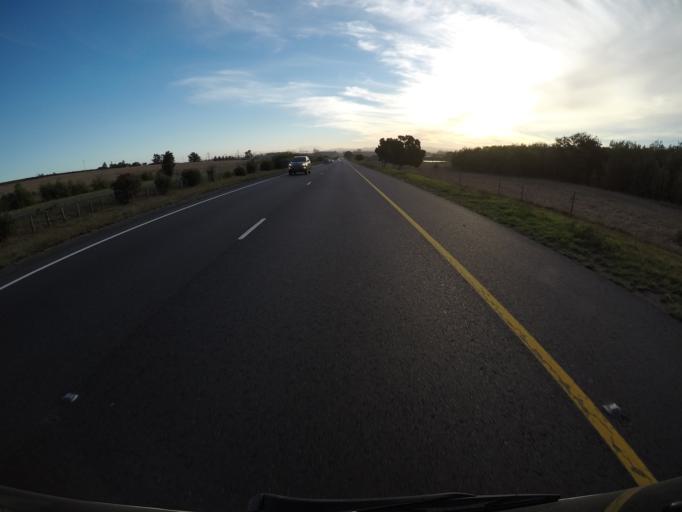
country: ZA
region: Western Cape
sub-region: City of Cape Town
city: Kraaifontein
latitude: -33.8129
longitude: 18.8161
